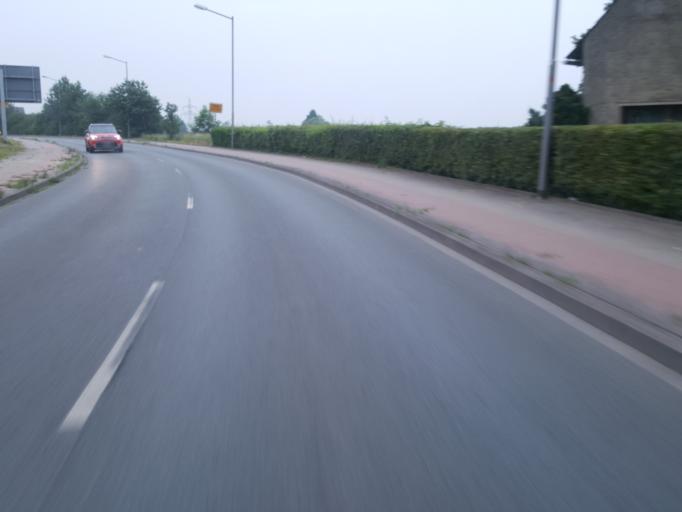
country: DE
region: North Rhine-Westphalia
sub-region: Regierungsbezirk Detmold
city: Kirchlengern
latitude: 52.1936
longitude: 8.6243
